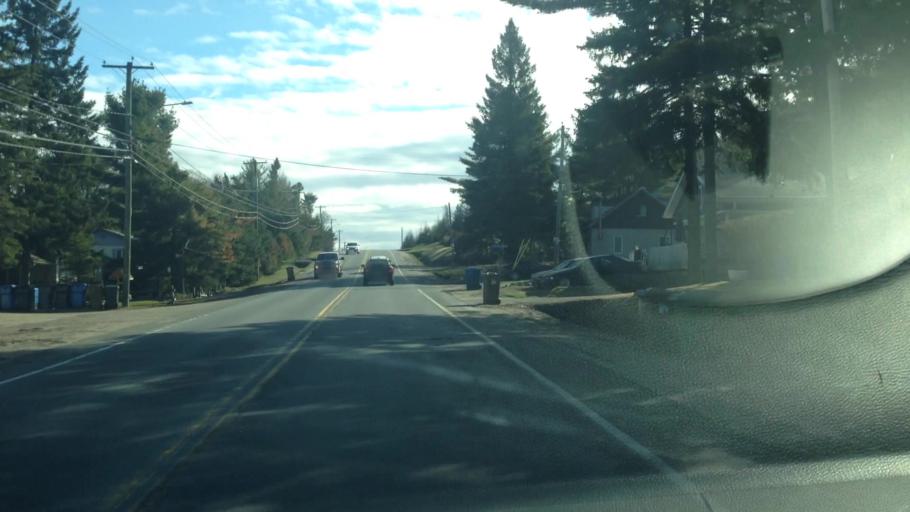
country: CA
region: Quebec
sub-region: Laurentides
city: Sainte-Adele
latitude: 46.0224
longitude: -74.0725
